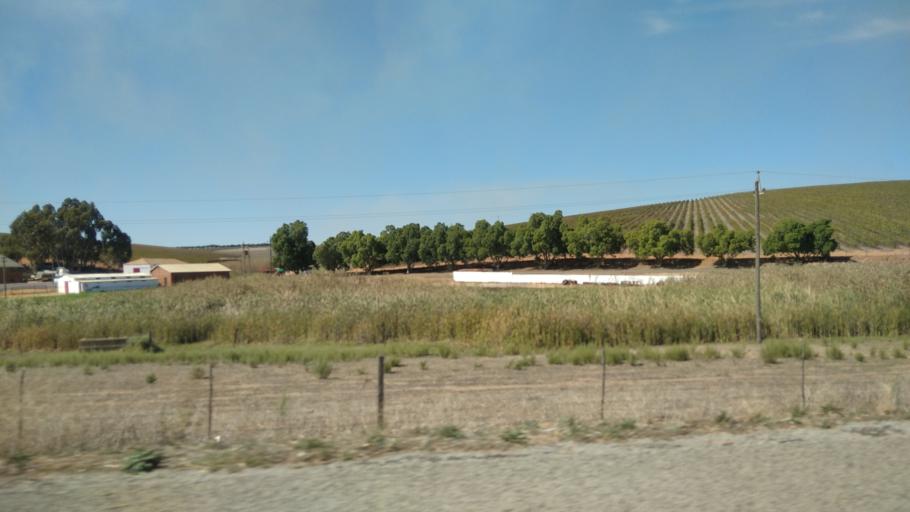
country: ZA
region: Western Cape
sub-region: West Coast District Municipality
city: Malmesbury
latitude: -33.4015
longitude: 18.6921
